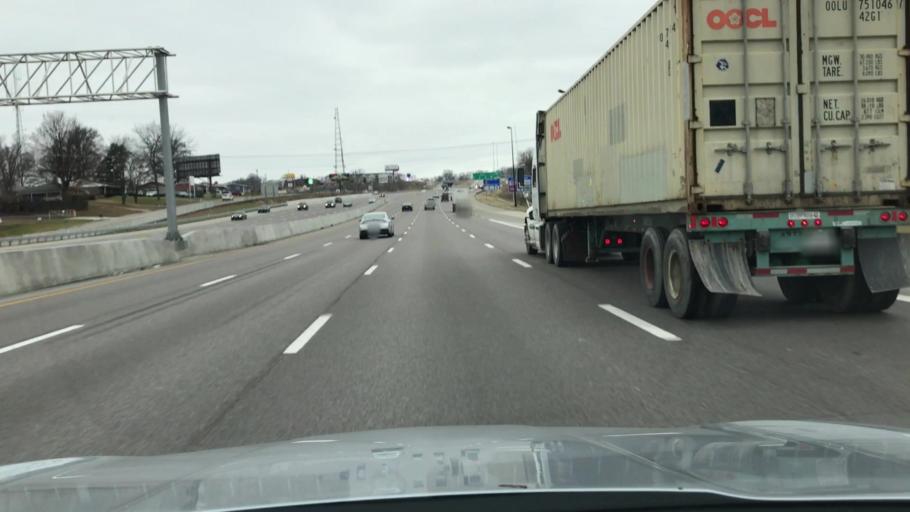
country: US
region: Missouri
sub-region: Saint Charles County
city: Saint Charles
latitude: 38.7720
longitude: -90.5029
